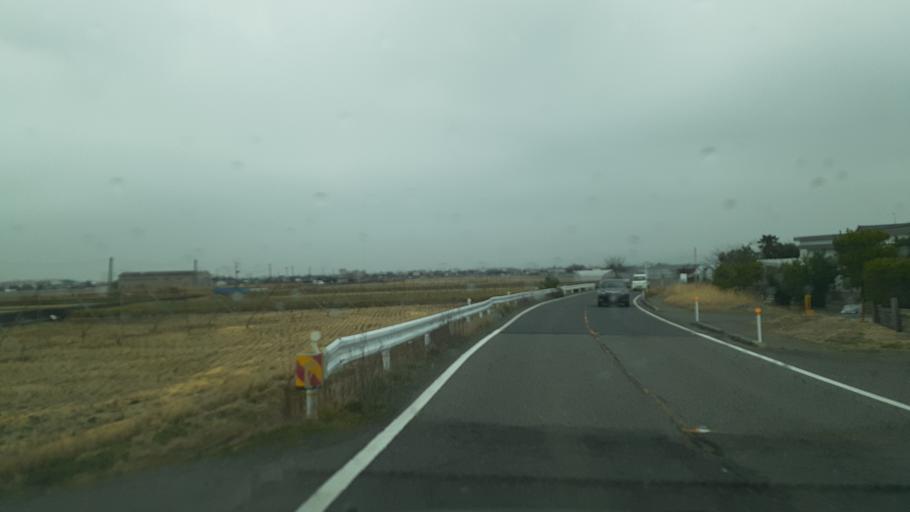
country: JP
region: Niigata
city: Kameda-honcho
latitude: 37.8631
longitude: 139.0662
